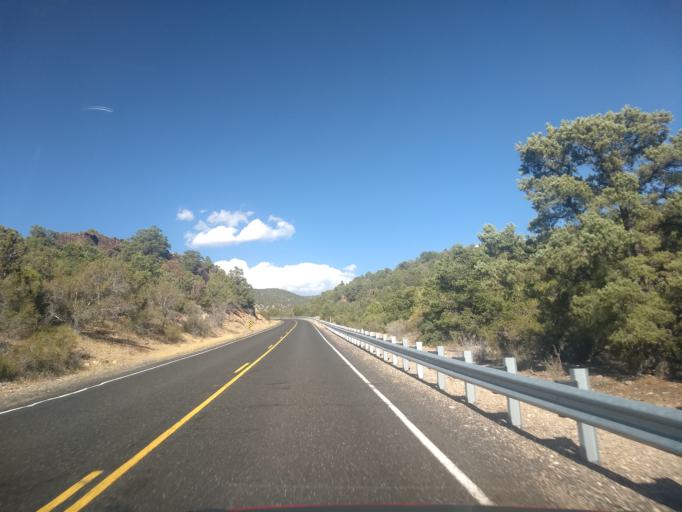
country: US
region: Utah
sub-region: Washington County
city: Enterprise
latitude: 37.4197
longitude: -113.5939
